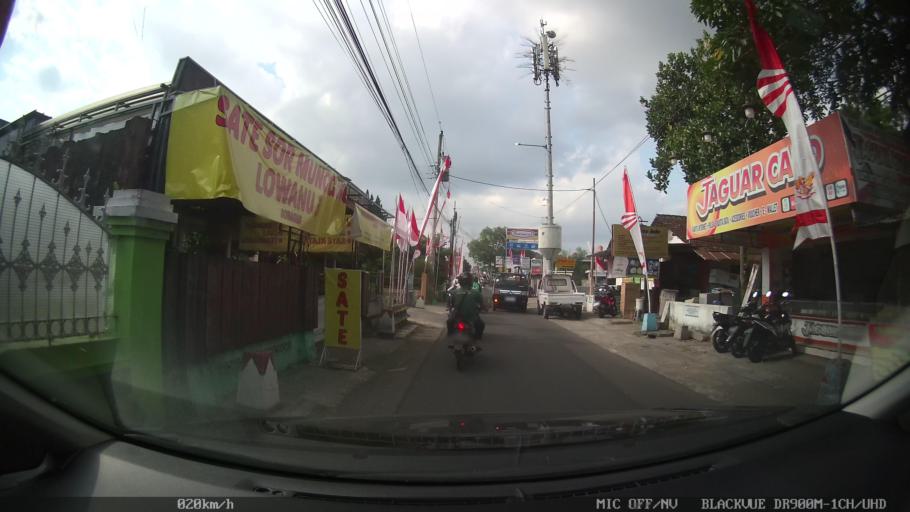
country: ID
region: Daerah Istimewa Yogyakarta
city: Yogyakarta
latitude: -7.7900
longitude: 110.3480
